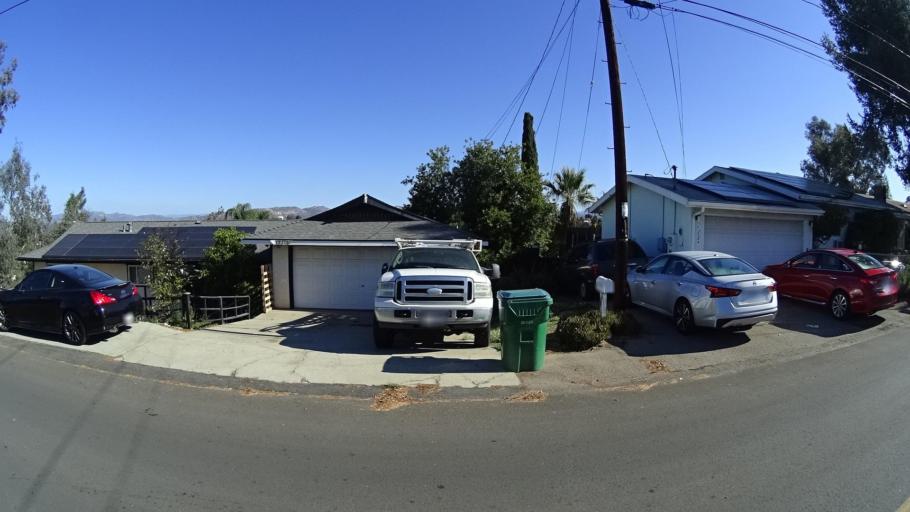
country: US
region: California
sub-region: San Diego County
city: Winter Gardens
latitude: 32.8320
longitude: -116.9279
